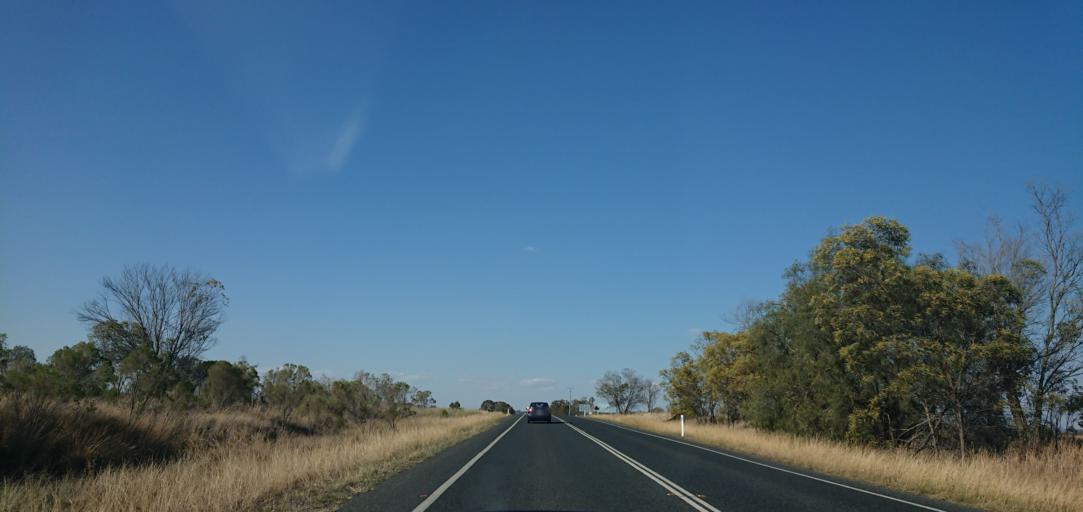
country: AU
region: Queensland
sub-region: Toowoomba
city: Westbrook
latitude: -27.6446
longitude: 151.7317
